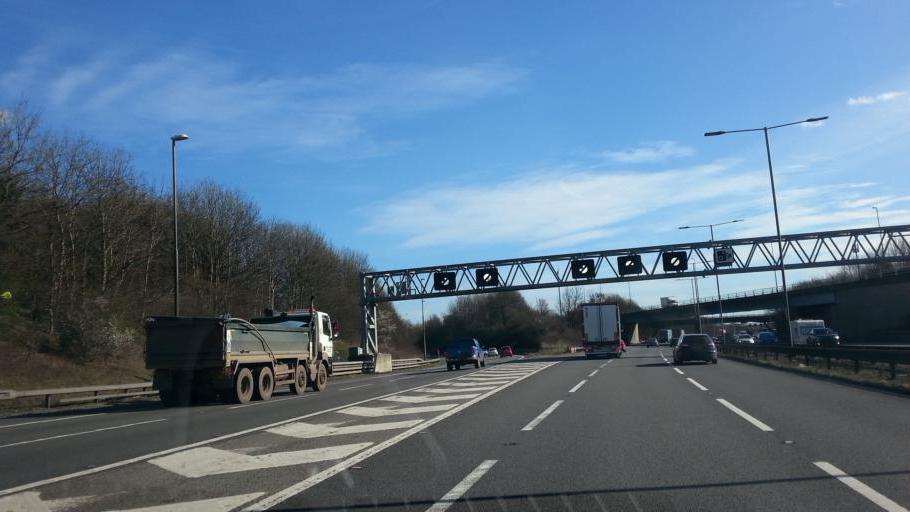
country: GB
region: England
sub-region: Warwickshire
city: Water Orton
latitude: 52.5090
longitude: -1.7455
